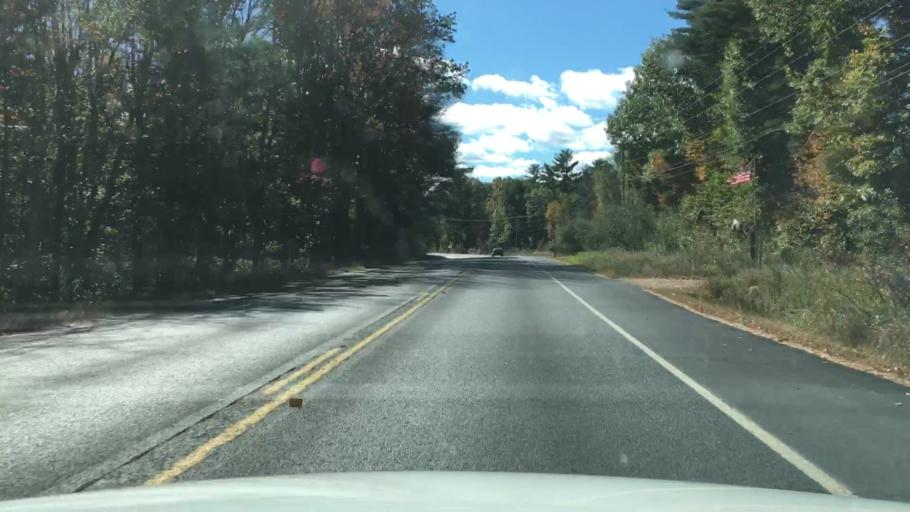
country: US
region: Maine
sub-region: York County
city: Alfred
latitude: 43.4469
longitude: -70.7286
